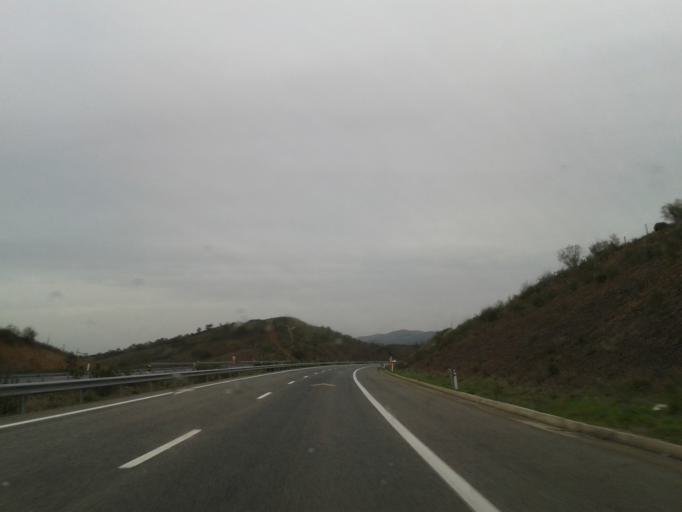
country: PT
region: Faro
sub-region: Silves
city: Sao Bartolomeu de Messines
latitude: 37.2805
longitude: -8.2645
